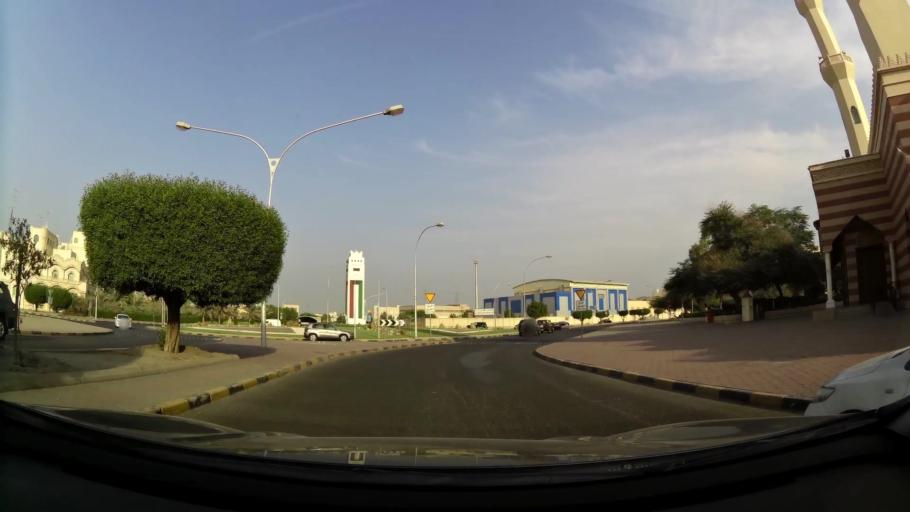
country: KW
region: Muhafazat Hawalli
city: Hawalli
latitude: 29.3130
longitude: 48.0047
